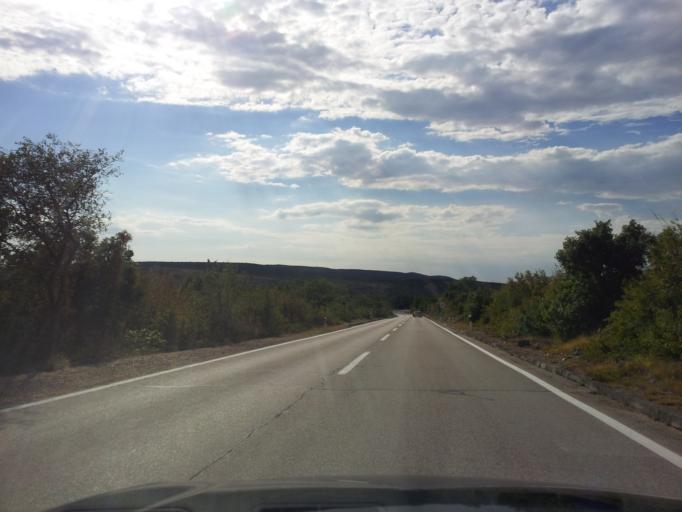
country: HR
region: Zadarska
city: Posedarje
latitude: 44.2290
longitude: 15.5354
